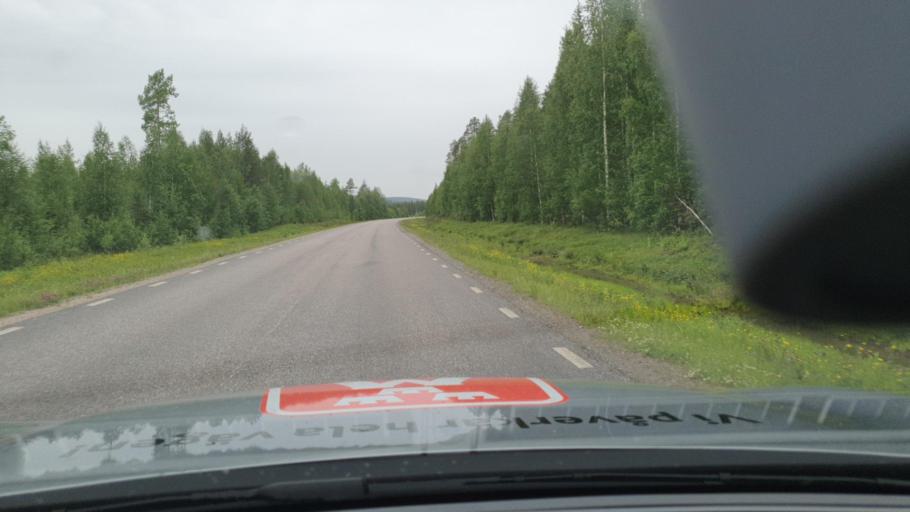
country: SE
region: Norrbotten
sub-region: Overtornea Kommun
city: OEvertornea
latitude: 66.3979
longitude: 23.5145
